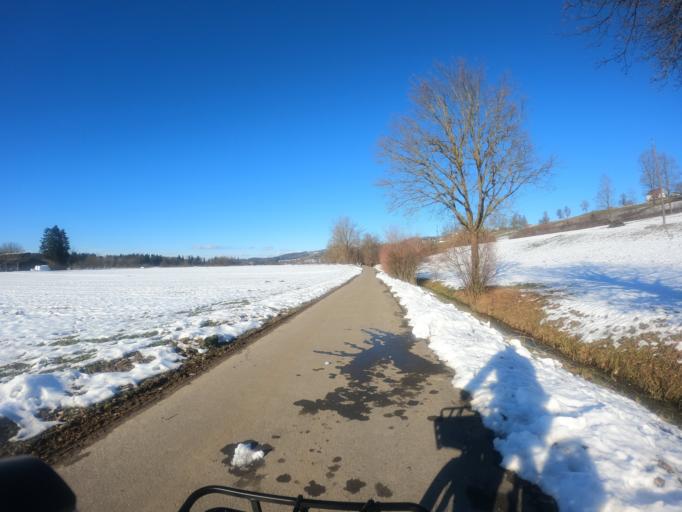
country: CH
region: Aargau
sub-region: Bezirk Bremgarten
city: Oberlunkhofen
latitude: 47.3045
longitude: 8.3872
